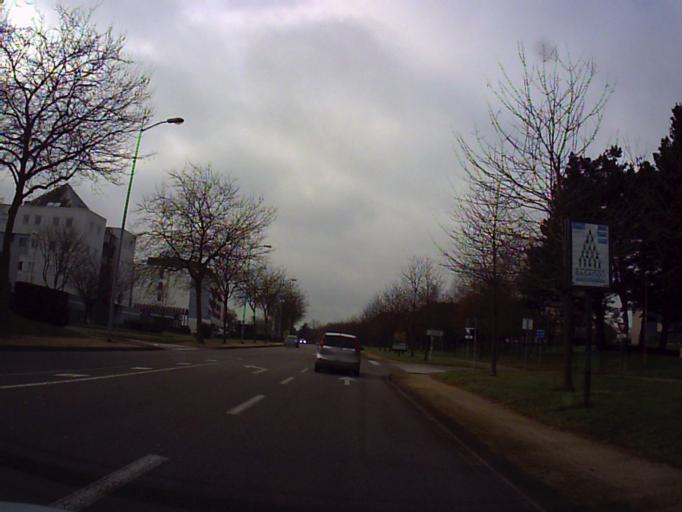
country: FR
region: Brittany
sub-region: Departement du Morbihan
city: Vannes
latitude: 47.6569
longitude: -2.7821
